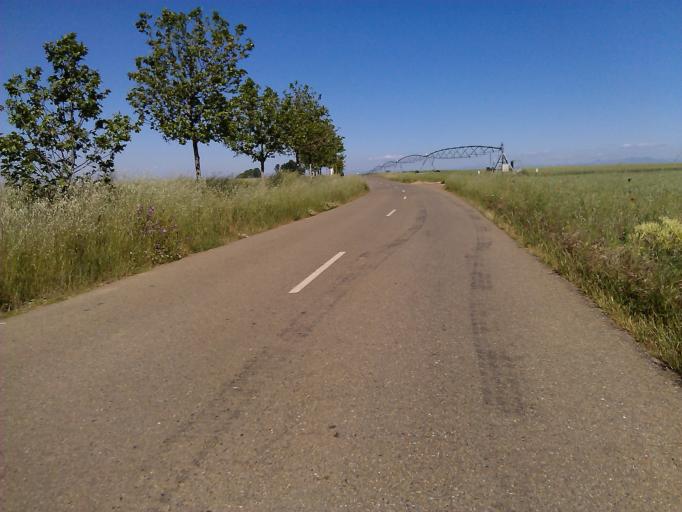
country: ES
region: Castille and Leon
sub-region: Provincia de Leon
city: Villamoratiel de las Matas
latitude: 42.4308
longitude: -5.2365
